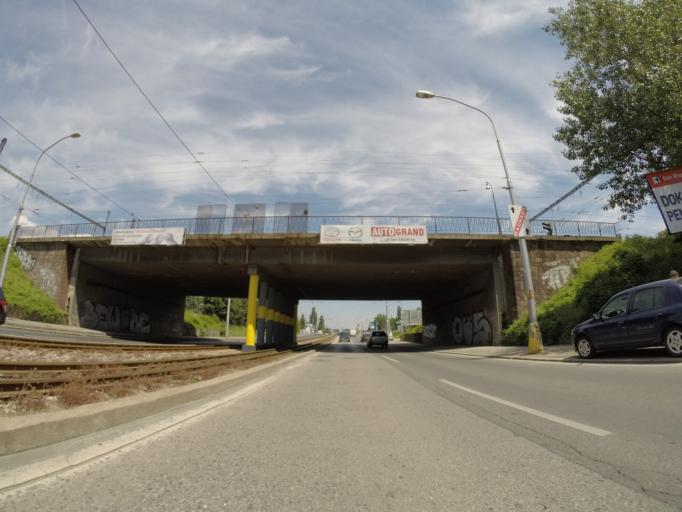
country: SK
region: Bratislavsky
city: Bratislava
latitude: 48.1734
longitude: 17.1429
